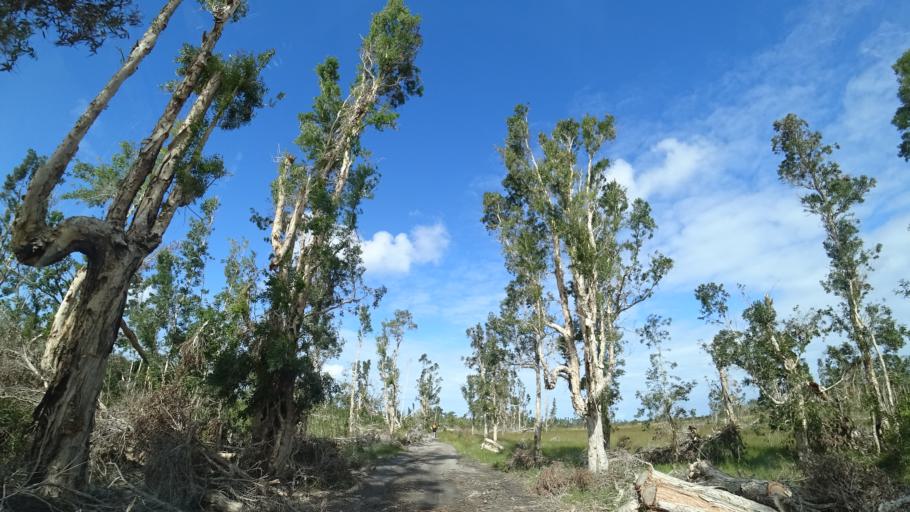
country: MZ
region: Sofala
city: Beira
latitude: -19.5713
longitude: 35.2529
